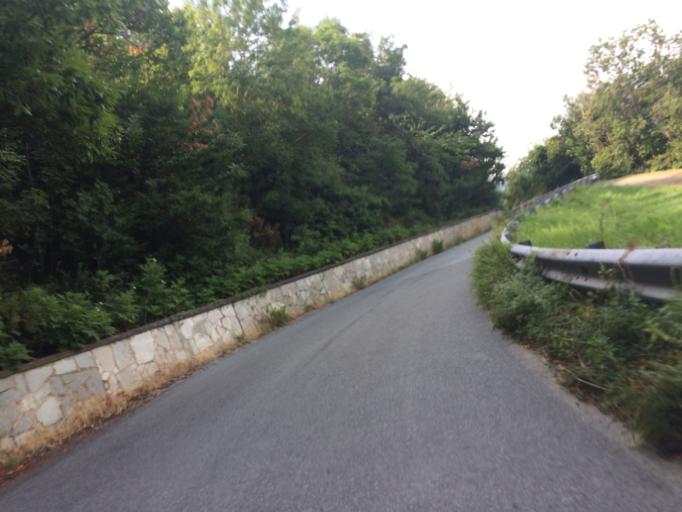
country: IT
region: Liguria
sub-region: Provincia di Savona
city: San Giovanni
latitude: 44.3933
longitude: 8.5109
